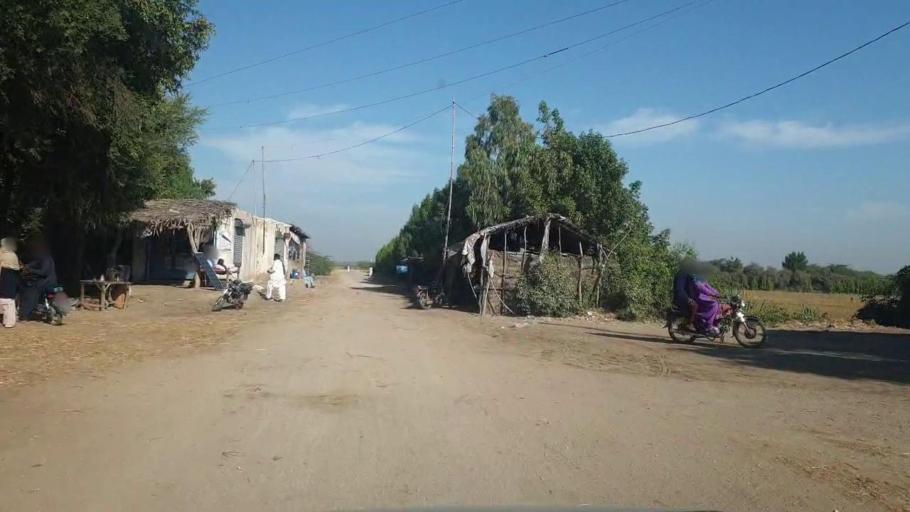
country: PK
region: Sindh
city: Talhar
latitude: 24.9450
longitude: 68.7870
